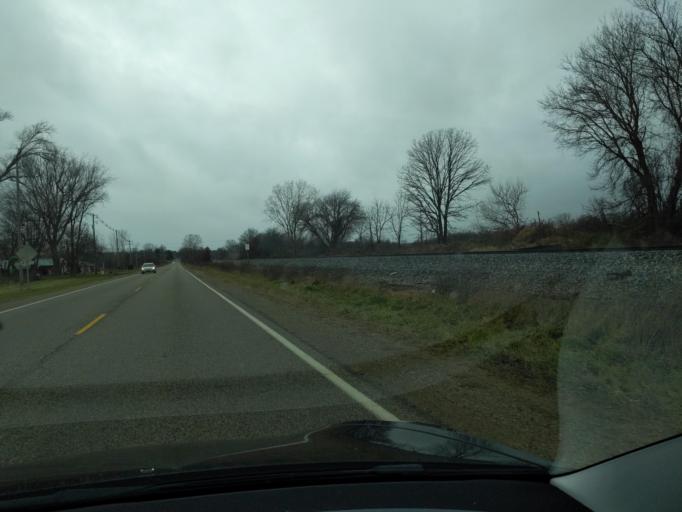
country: US
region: Michigan
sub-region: Jackson County
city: Spring Arbor
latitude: 42.2538
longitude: -84.5003
